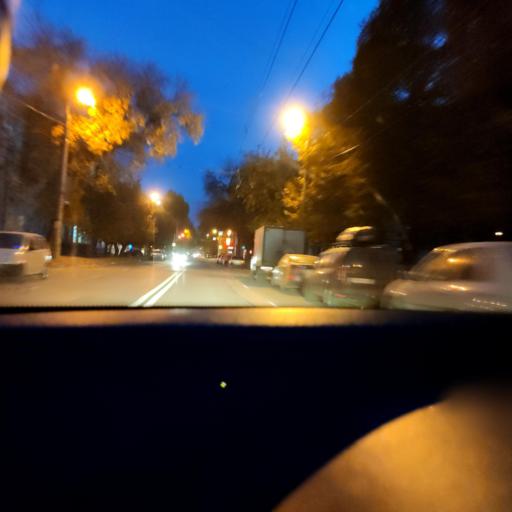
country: RU
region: Samara
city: Samara
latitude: 53.2117
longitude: 50.2424
